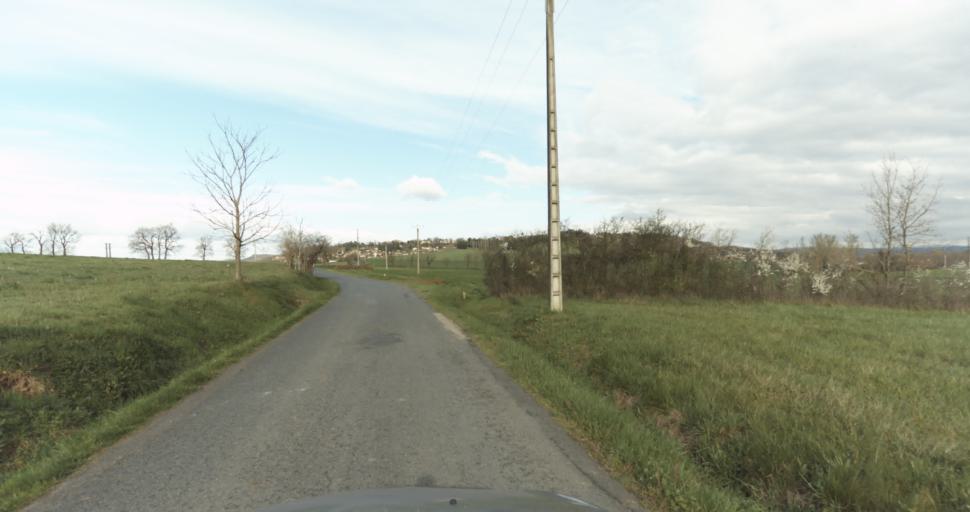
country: FR
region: Midi-Pyrenees
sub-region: Departement du Tarn
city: Puygouzon
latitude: 43.8895
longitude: 2.1885
